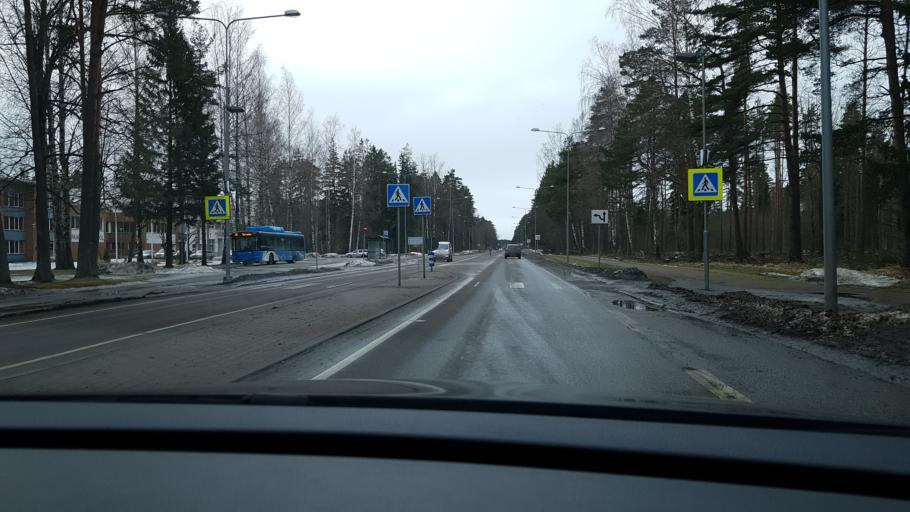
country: EE
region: Paernumaa
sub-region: Paikuse vald
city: Paikuse
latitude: 58.3731
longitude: 24.6133
